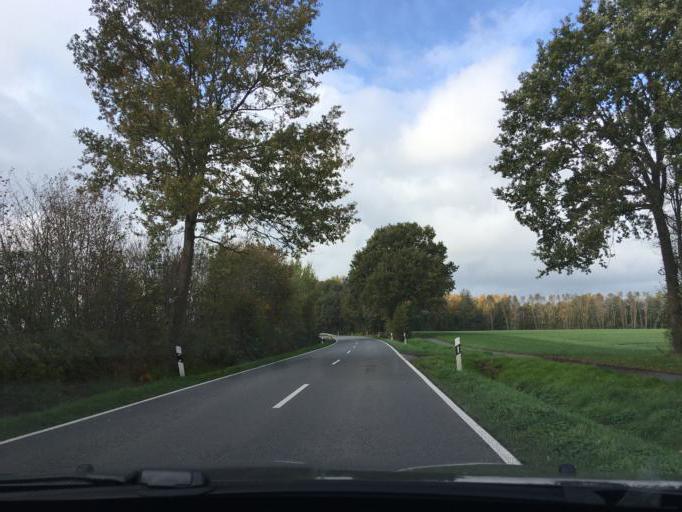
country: DE
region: North Rhine-Westphalia
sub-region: Regierungsbezirk Munster
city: Vreden
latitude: 52.0535
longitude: 6.7727
